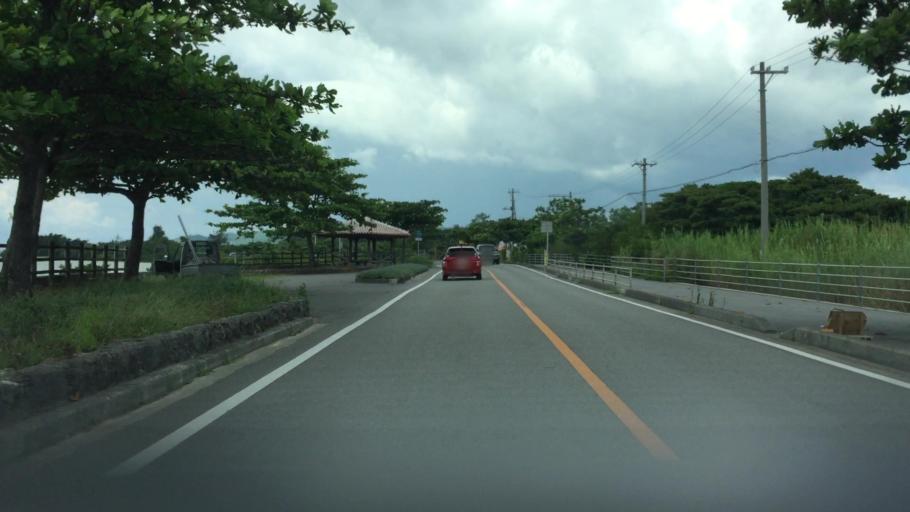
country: JP
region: Okinawa
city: Ishigaki
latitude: 24.4141
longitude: 124.1426
